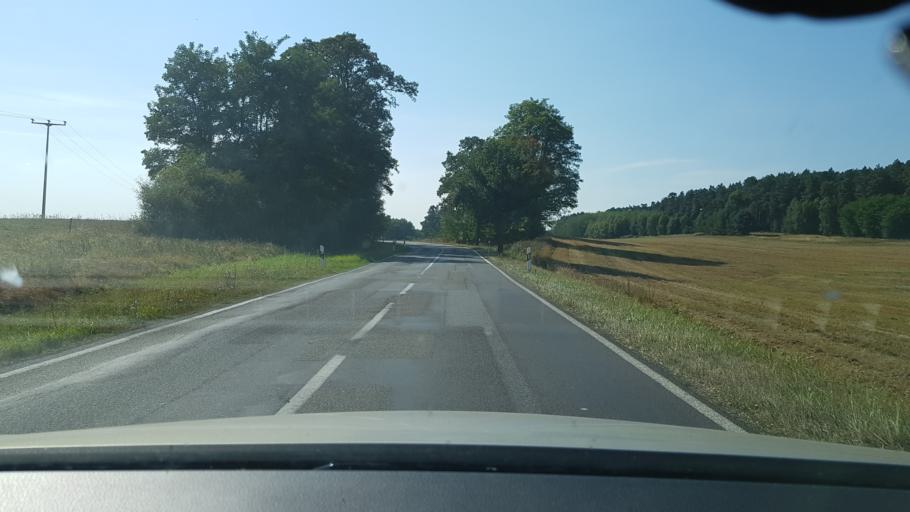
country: DE
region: Brandenburg
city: Lawitz
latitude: 52.1145
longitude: 14.5892
